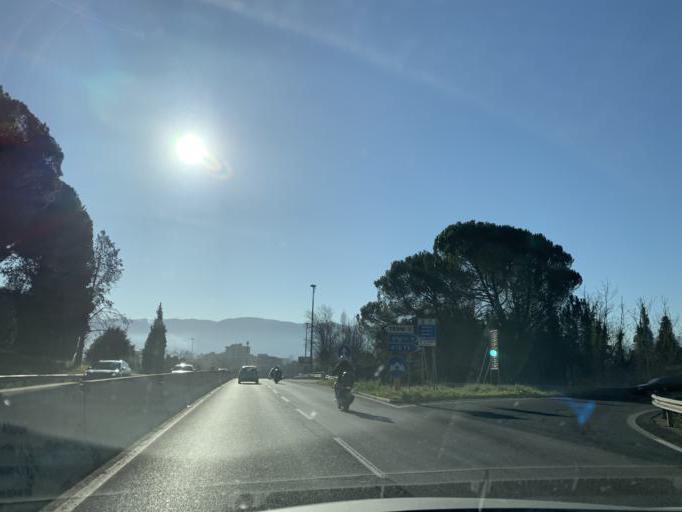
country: IT
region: Umbria
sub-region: Provincia di Terni
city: Terni
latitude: 42.5735
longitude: 12.6279
